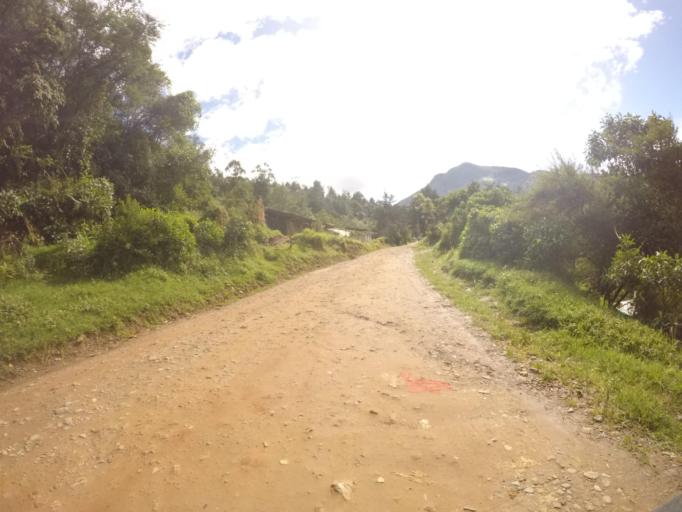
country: CO
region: Cauca
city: Silvia
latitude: 2.6380
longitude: -76.3686
